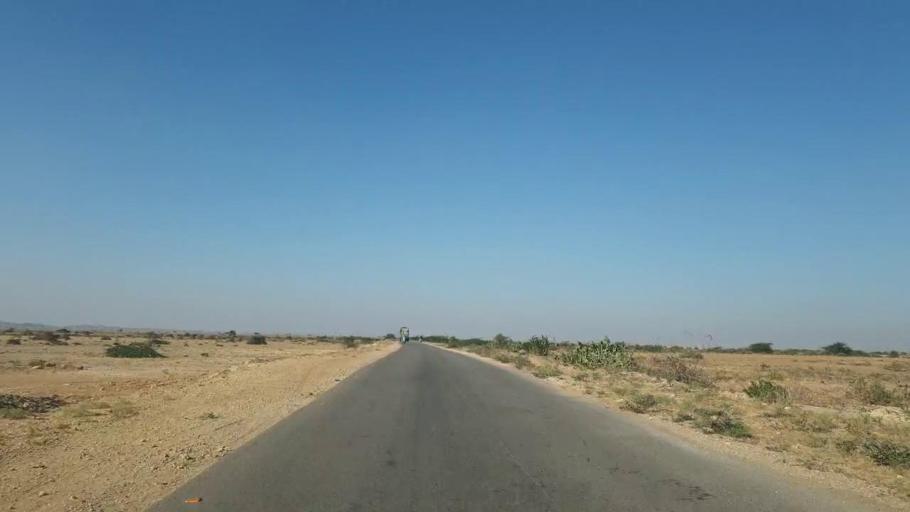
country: PK
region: Sindh
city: Malir Cantonment
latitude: 25.2500
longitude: 67.6042
